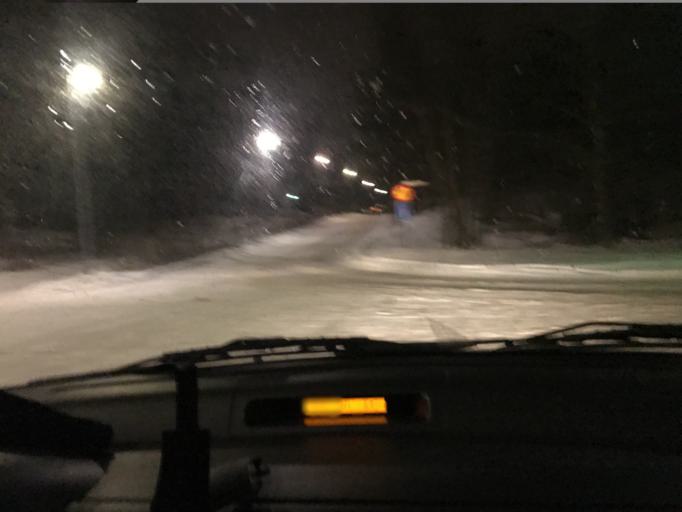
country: SE
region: Stockholm
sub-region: Nacka Kommun
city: Fisksatra
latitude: 59.3138
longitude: 18.2449
